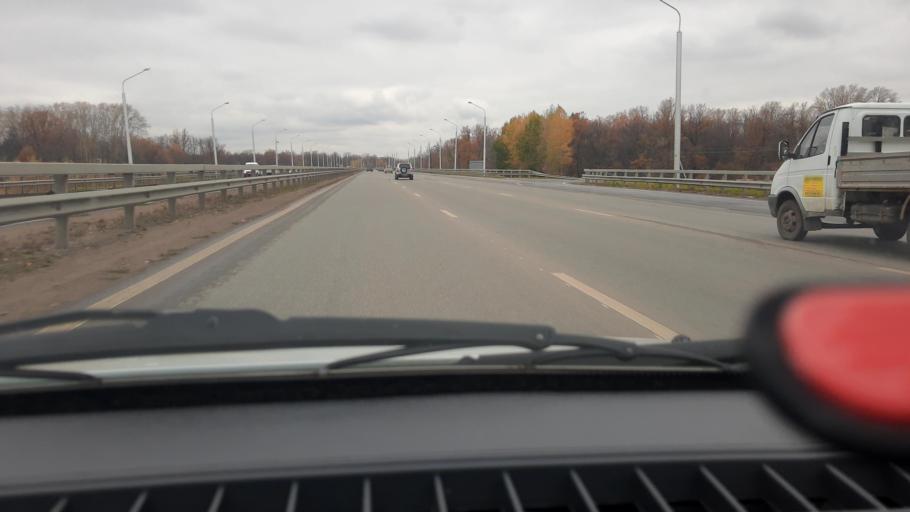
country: RU
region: Bashkortostan
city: Mikhaylovka
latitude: 54.7794
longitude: 55.9274
